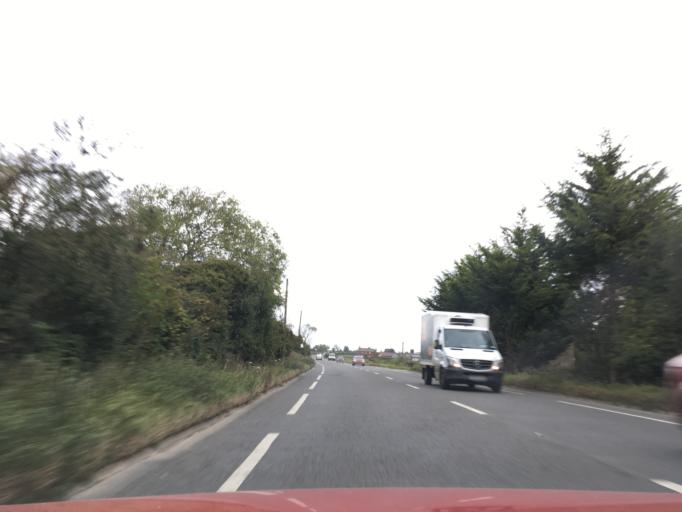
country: GB
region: England
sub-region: Gloucestershire
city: Dursley
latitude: 51.7408
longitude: -2.3550
